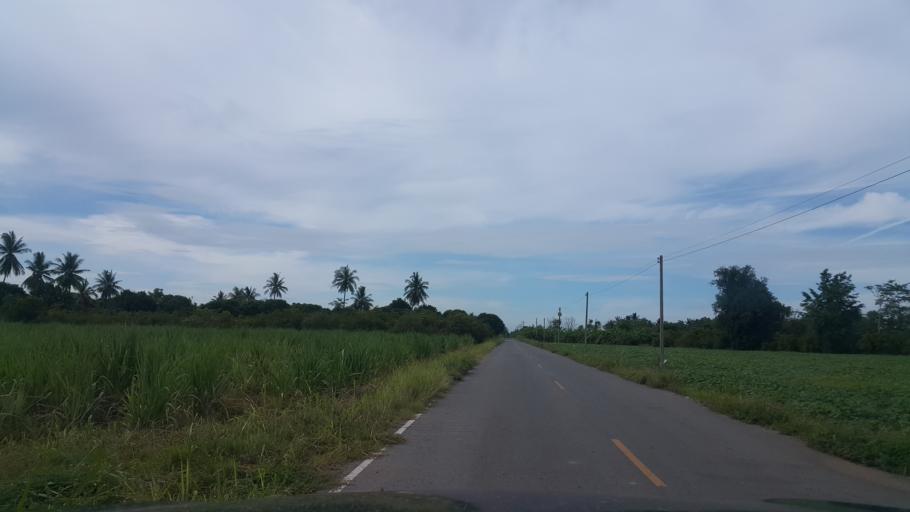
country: TH
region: Sukhothai
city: Sawankhalok
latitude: 17.2740
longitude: 99.9059
